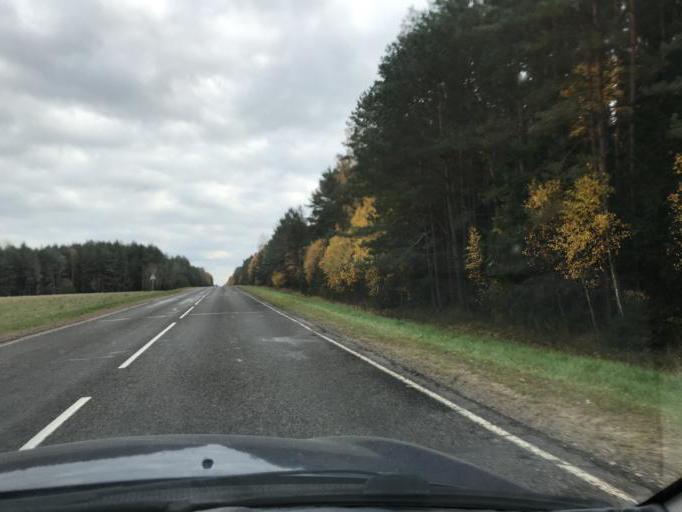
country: BY
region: Grodnenskaya
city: Lida
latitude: 53.7463
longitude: 25.2961
